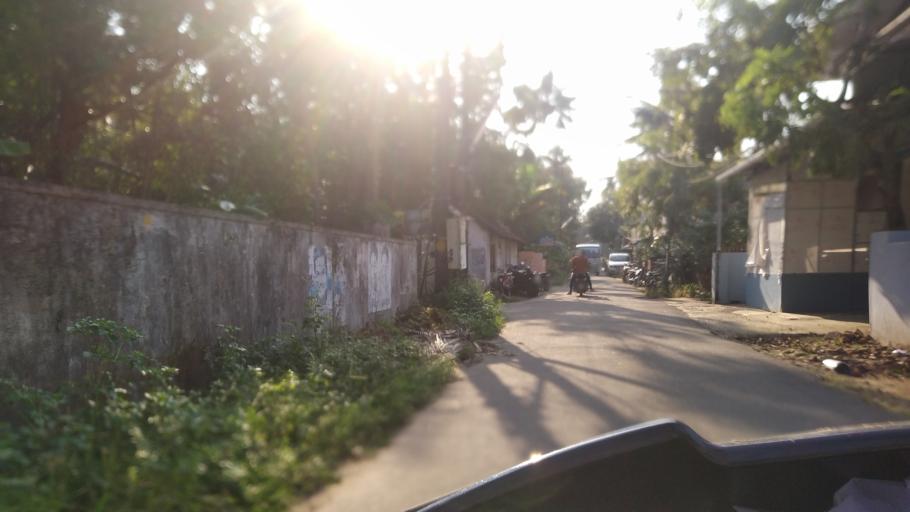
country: IN
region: Kerala
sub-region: Ernakulam
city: Elur
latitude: 10.0467
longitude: 76.2245
